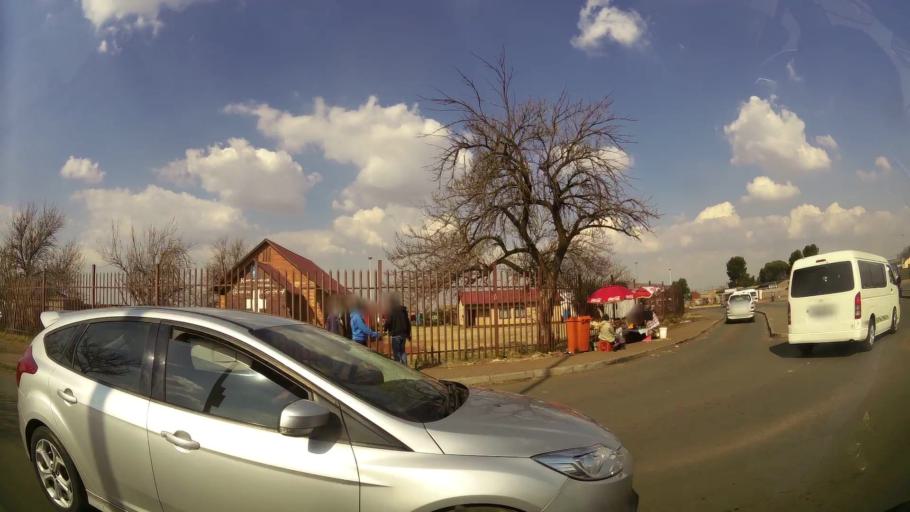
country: ZA
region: Gauteng
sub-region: Ekurhuleni Metropolitan Municipality
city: Germiston
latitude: -26.3279
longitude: 28.1517
